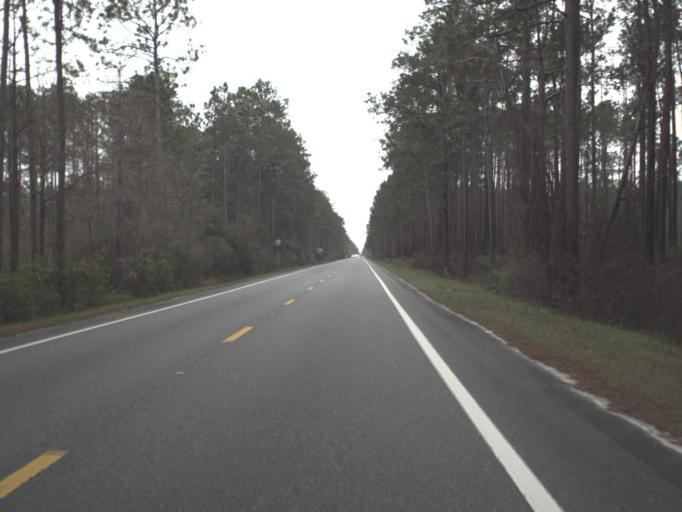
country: US
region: Florida
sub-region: Franklin County
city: Apalachicola
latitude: 29.9609
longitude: -84.9761
